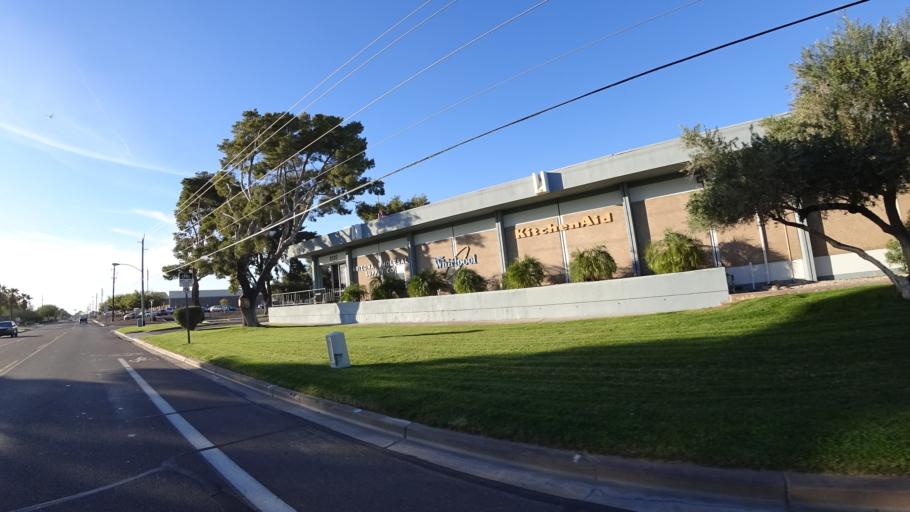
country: US
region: Arizona
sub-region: Maricopa County
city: Phoenix
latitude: 33.4239
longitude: -112.0384
